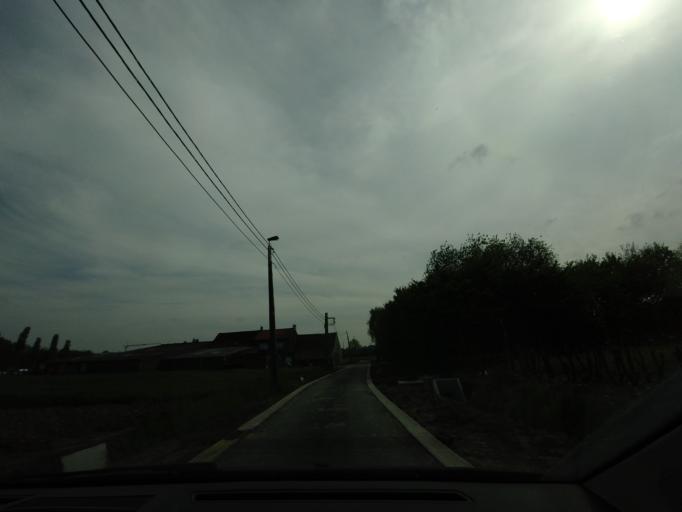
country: BE
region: Flanders
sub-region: Provincie Antwerpen
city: Kontich
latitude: 51.1098
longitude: 4.4629
